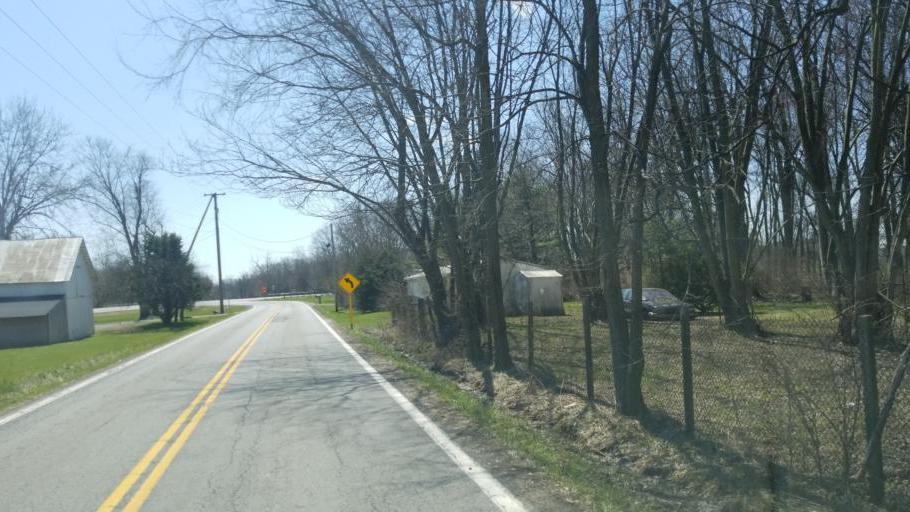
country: US
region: Ohio
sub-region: Marion County
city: Prospect
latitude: 40.4860
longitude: -83.1906
